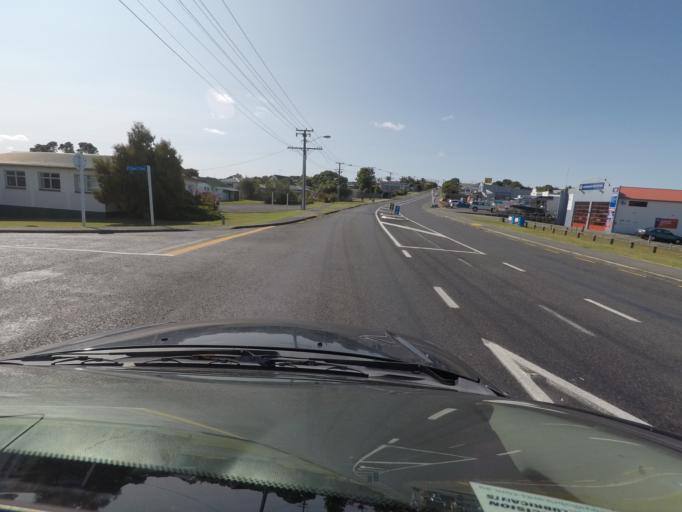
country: NZ
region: Auckland
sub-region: Auckland
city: Warkworth
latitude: -36.4228
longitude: 174.7264
